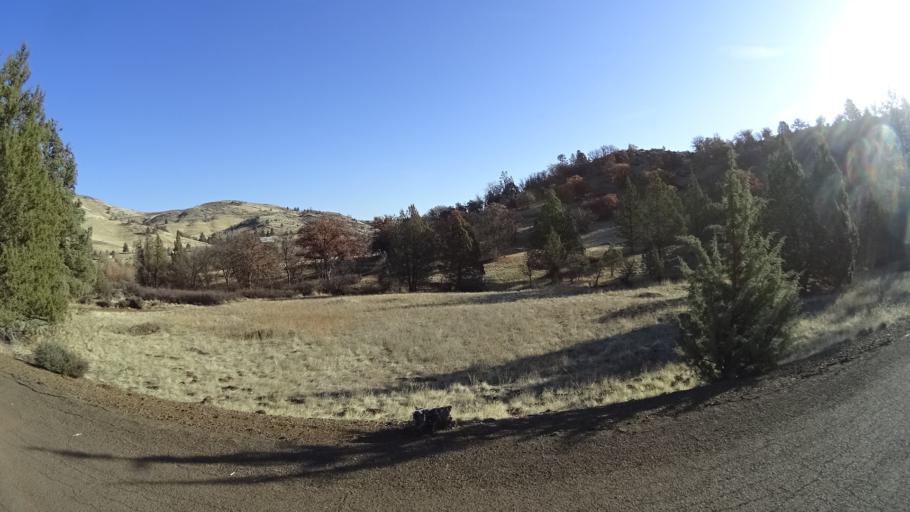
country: US
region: California
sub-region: Siskiyou County
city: Montague
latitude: 41.8955
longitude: -122.5011
